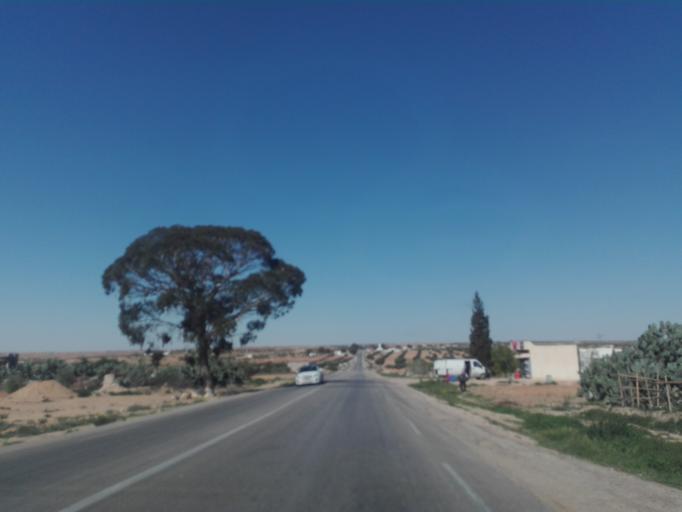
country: TN
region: Safaqis
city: Bi'r `Ali Bin Khalifah
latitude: 34.7411
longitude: 10.3832
